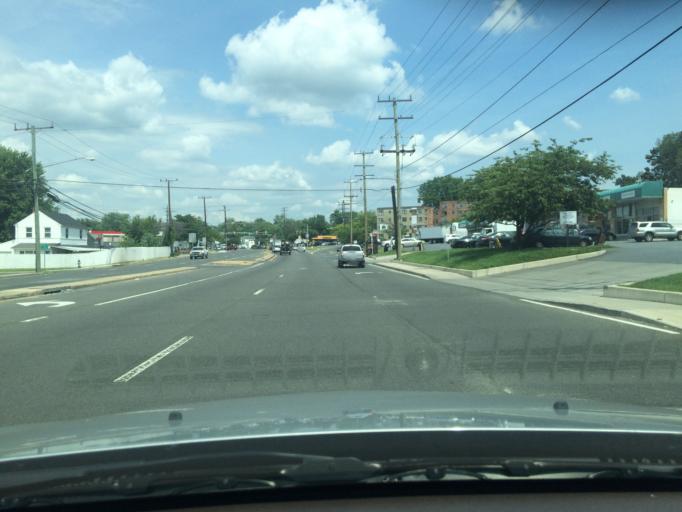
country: US
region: Maryland
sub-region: Prince George's County
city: Chillum
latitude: 38.9706
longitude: -76.9780
